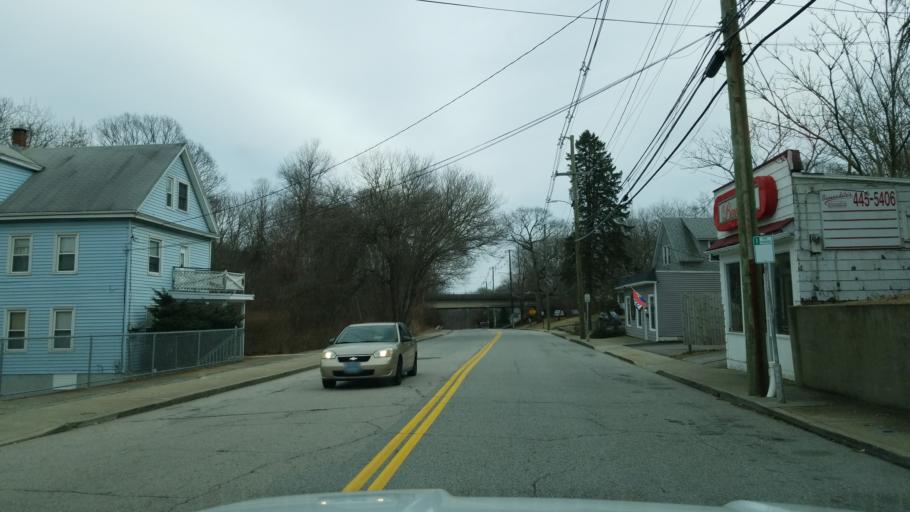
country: US
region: Connecticut
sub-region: New London County
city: Groton
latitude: 41.3459
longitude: -72.0710
